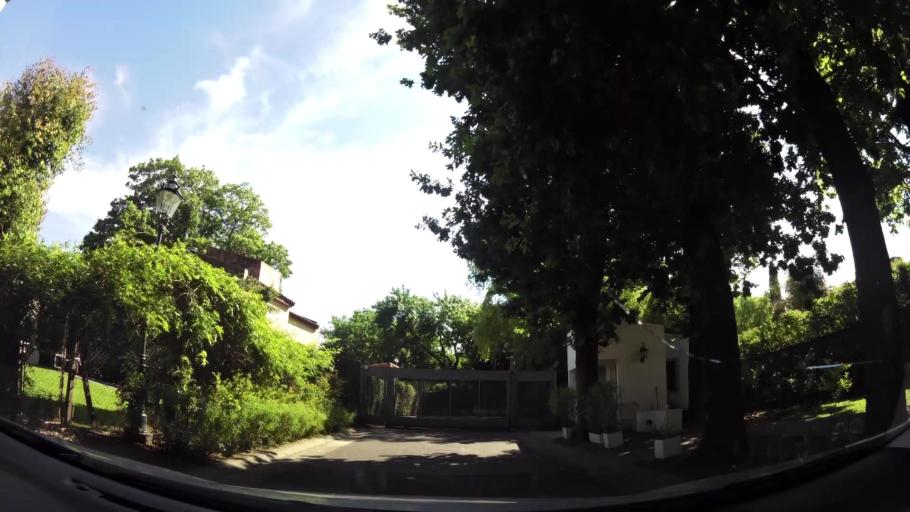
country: AR
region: Buenos Aires
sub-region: Partido de Tigre
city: Tigre
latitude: -34.4784
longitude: -58.5754
